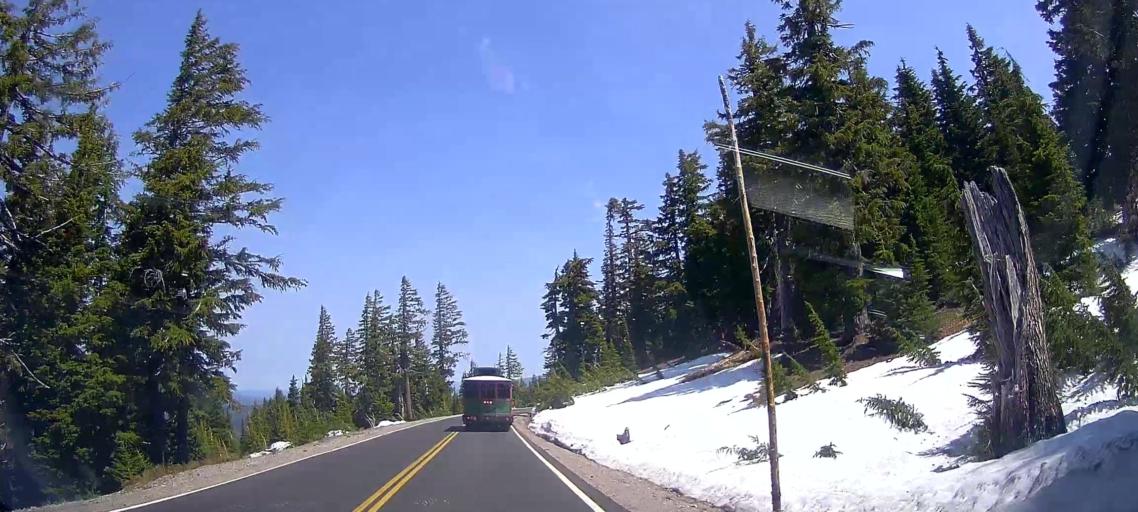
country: US
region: Oregon
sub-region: Jackson County
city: Shady Cove
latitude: 42.9771
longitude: -122.1431
